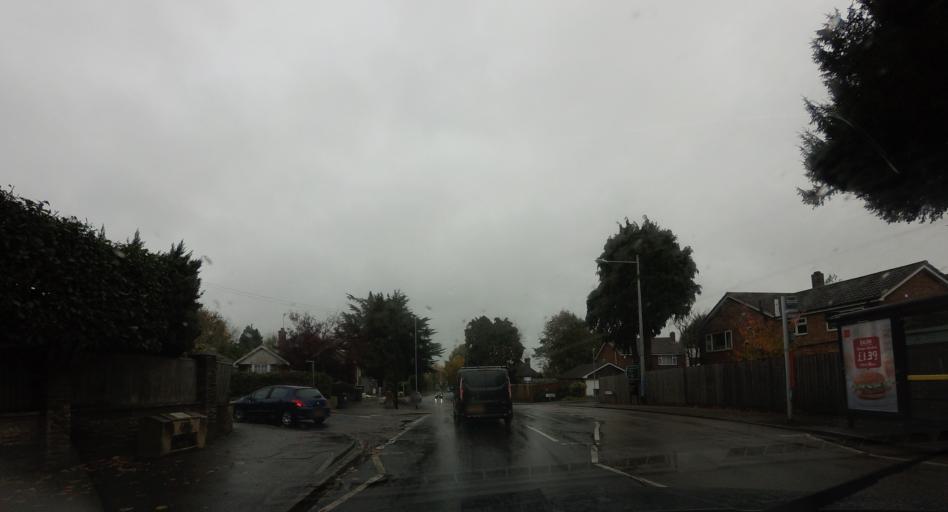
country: GB
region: England
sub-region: Kent
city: Tonbridge
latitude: 51.2025
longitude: 0.2861
